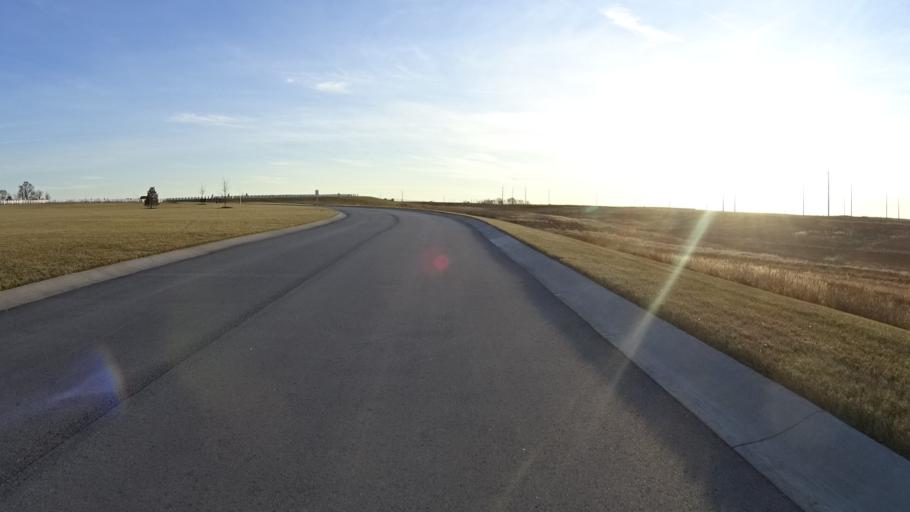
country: US
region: Nebraska
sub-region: Sarpy County
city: Chalco
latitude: 41.1365
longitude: -96.1342
